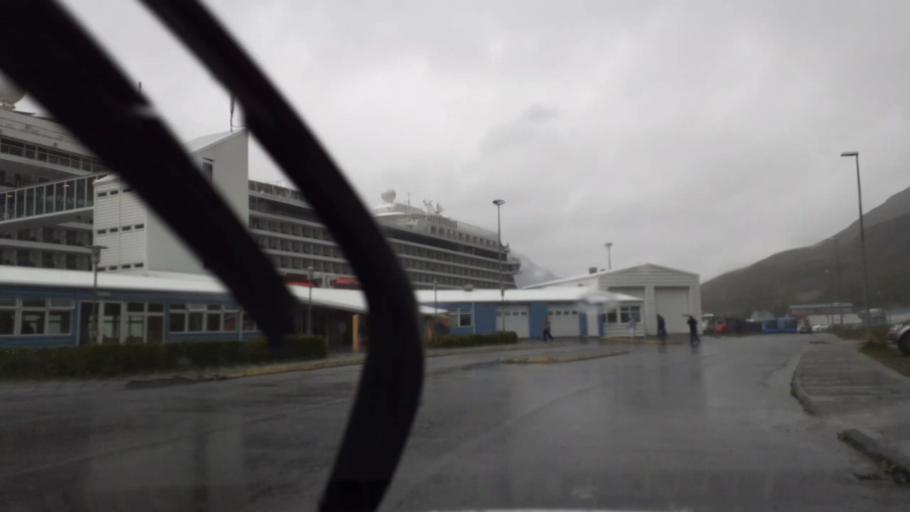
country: IS
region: East
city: Eskifjoerdur
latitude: 65.2629
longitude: -14.0023
